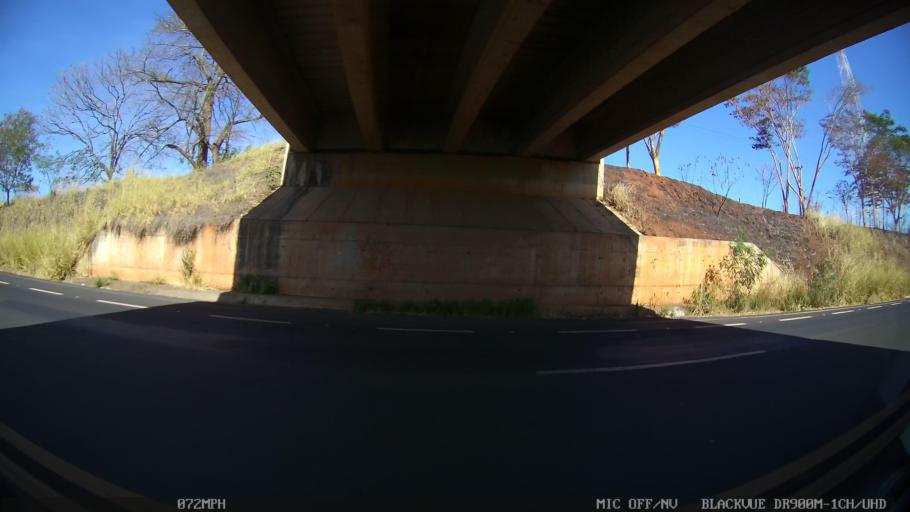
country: BR
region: Sao Paulo
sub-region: Barretos
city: Barretos
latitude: -20.6108
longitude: -48.7522
